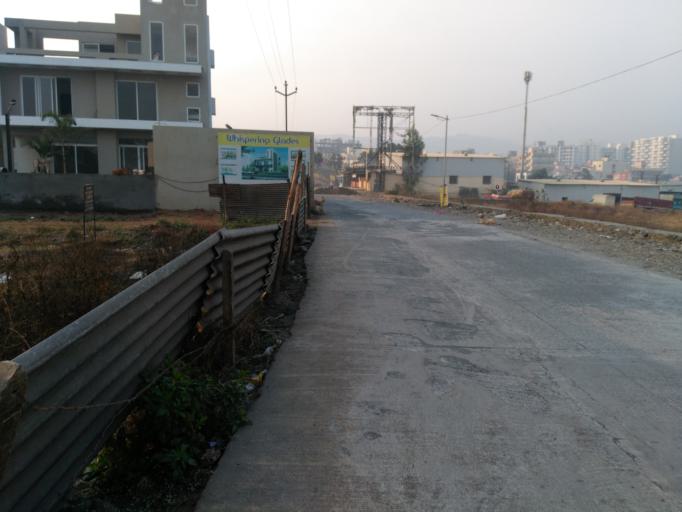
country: IN
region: Maharashtra
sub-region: Pune Division
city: Pune
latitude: 18.4518
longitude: 73.9110
